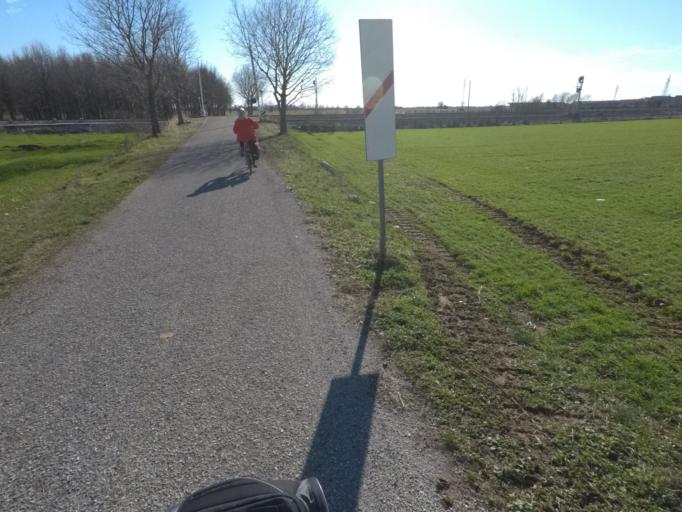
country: IT
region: Friuli Venezia Giulia
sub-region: Provincia di Udine
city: Cividale del Friuli
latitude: 46.0925
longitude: 13.4045
